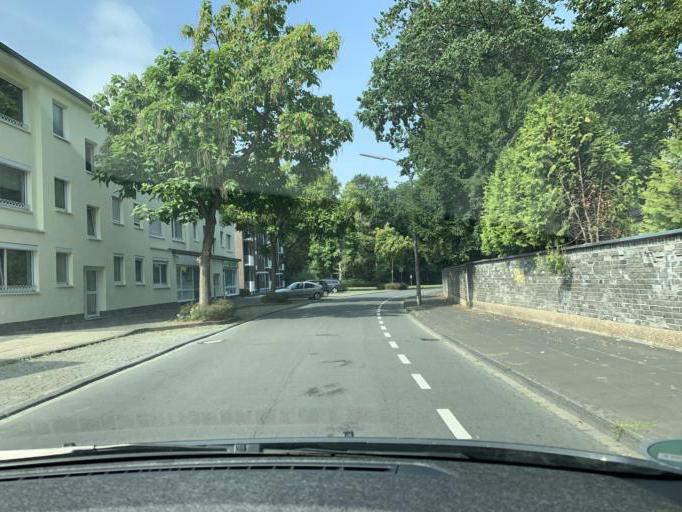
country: DE
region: North Rhine-Westphalia
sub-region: Regierungsbezirk Koln
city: Erftstadt
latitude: 50.8108
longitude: 6.8220
